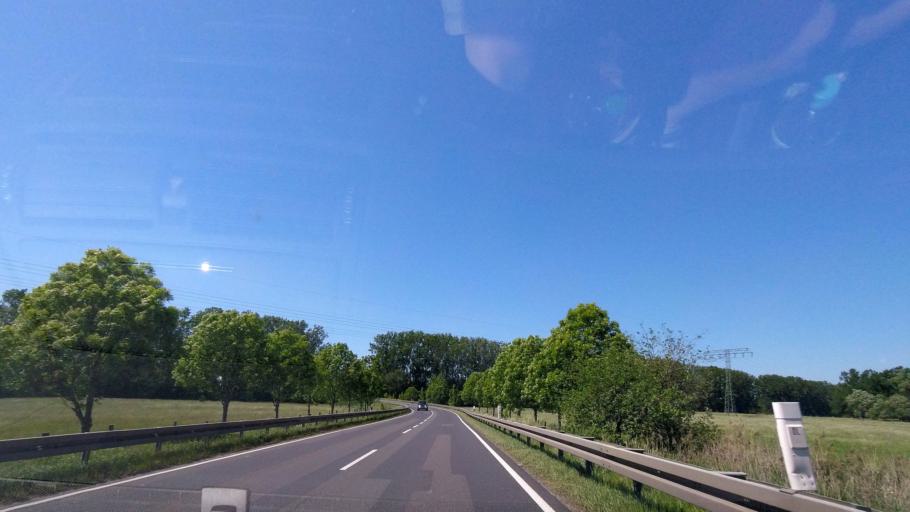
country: DE
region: Berlin
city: Wannsee
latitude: 52.3558
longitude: 13.1237
